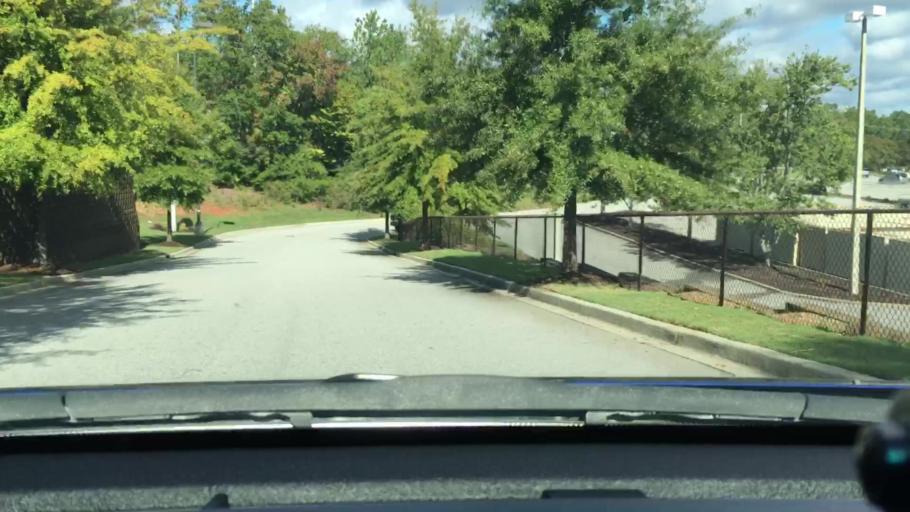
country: US
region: South Carolina
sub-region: Lexington County
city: Seven Oaks
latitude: 34.0658
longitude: -81.1661
